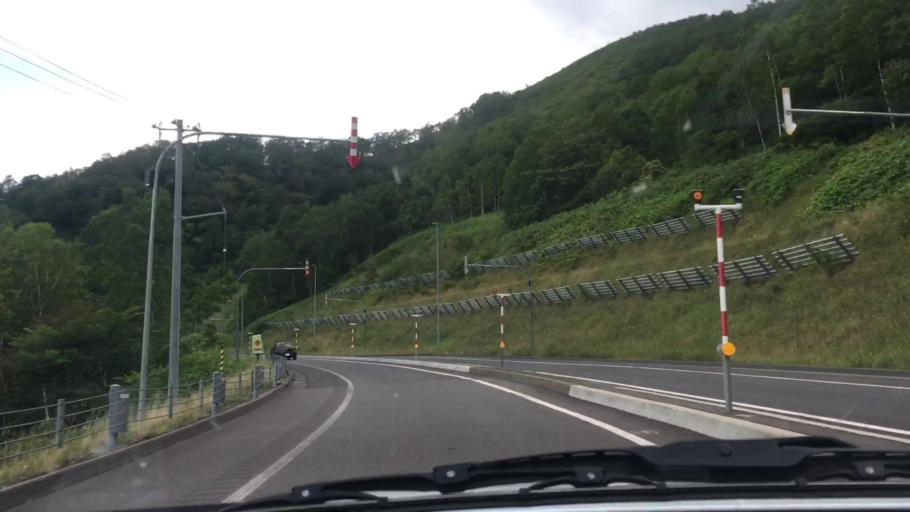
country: JP
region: Hokkaido
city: Shimo-furano
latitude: 43.1518
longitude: 142.7747
